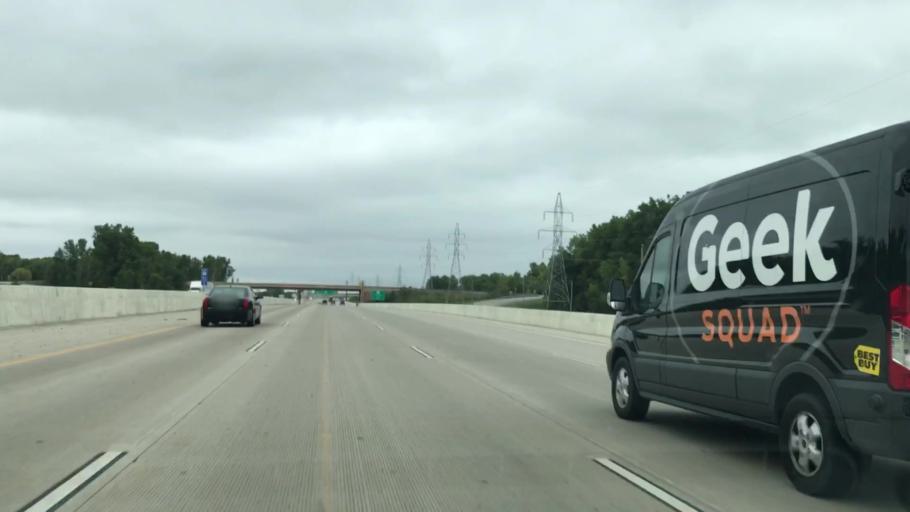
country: US
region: Wisconsin
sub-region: Brown County
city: Suamico
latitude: 44.5804
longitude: -88.0487
